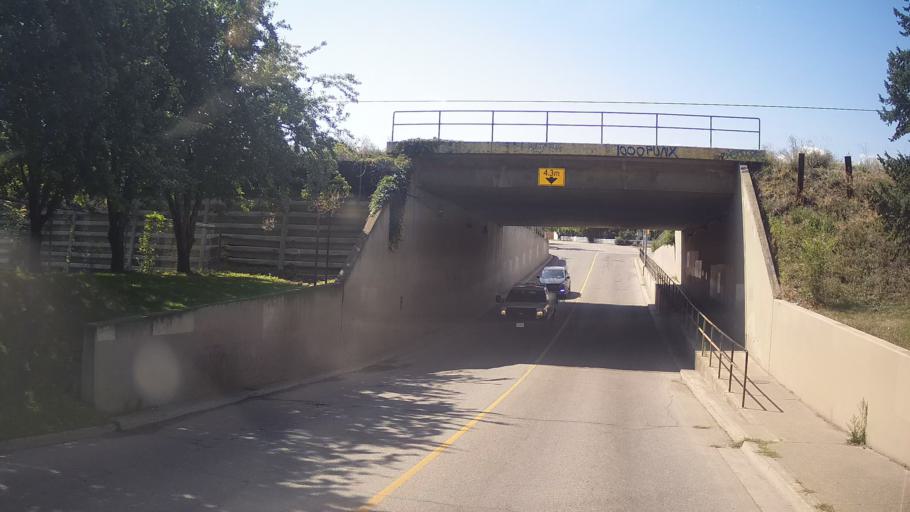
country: CA
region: British Columbia
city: Kamloops
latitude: 50.6753
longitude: -120.3158
